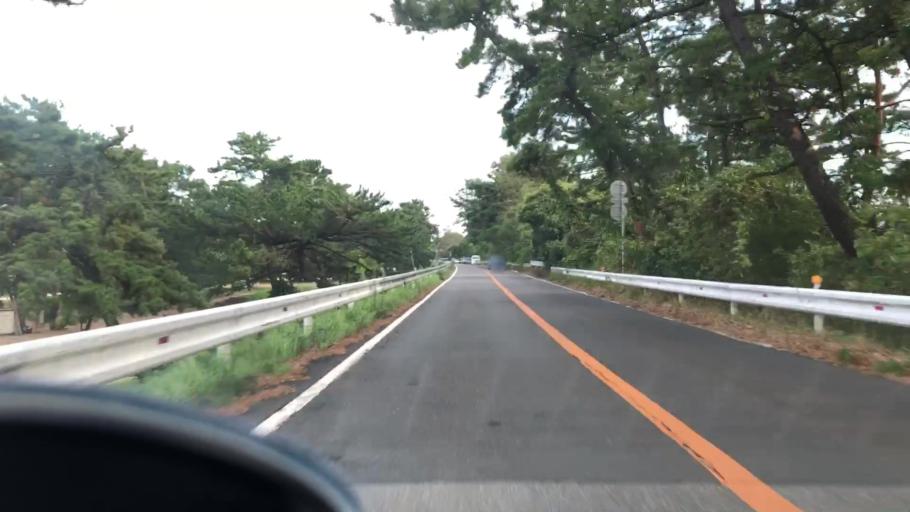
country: JP
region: Hyogo
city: Itami
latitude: 34.7571
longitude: 135.3720
